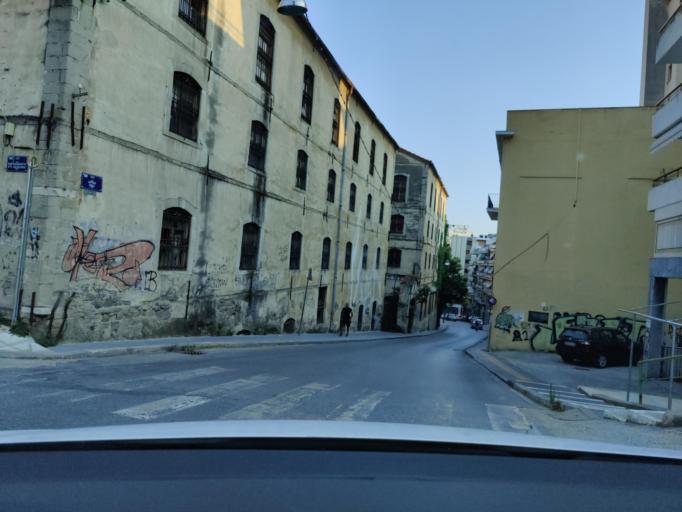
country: GR
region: East Macedonia and Thrace
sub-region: Nomos Kavalas
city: Kavala
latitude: 40.9382
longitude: 24.4060
